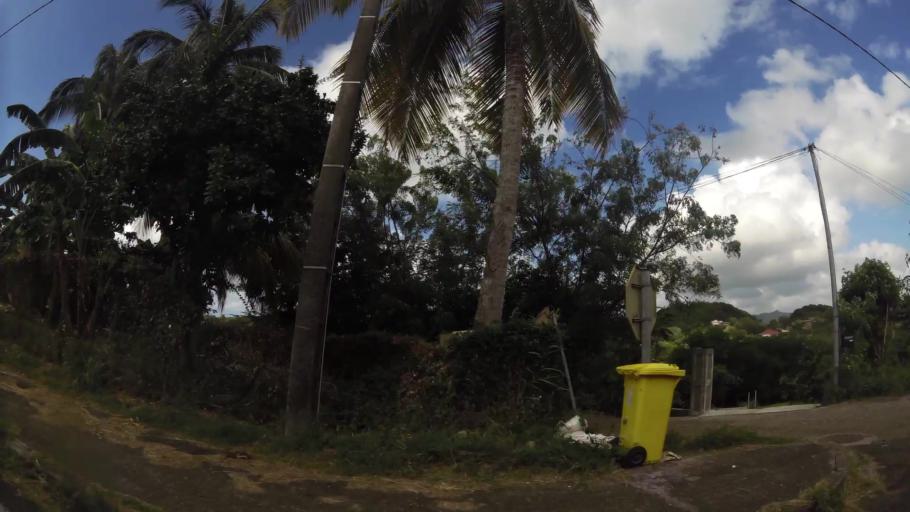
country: MQ
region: Martinique
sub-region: Martinique
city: Le Marin
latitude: 14.4475
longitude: -60.8633
